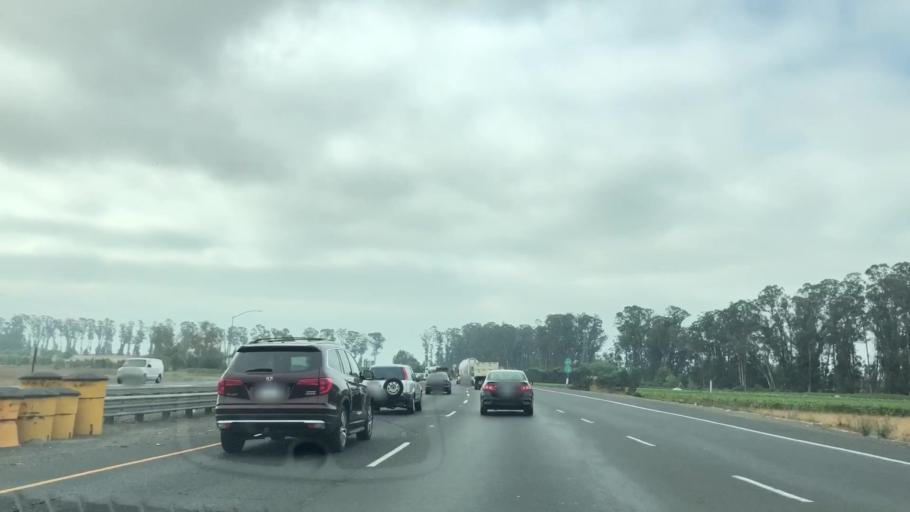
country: US
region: California
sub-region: Napa County
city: Napa
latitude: 38.2571
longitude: -122.3031
